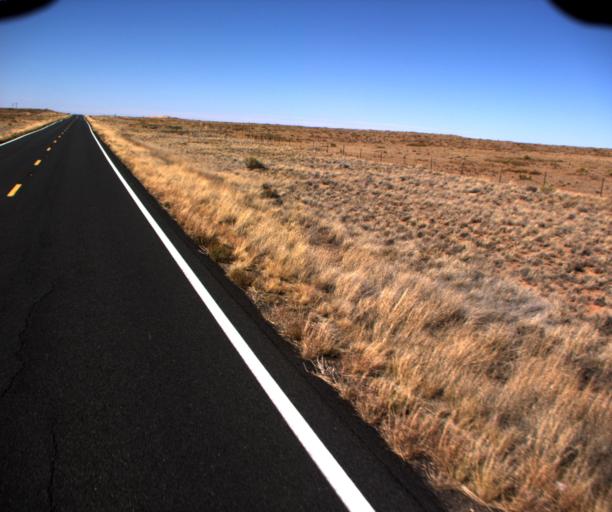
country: US
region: Arizona
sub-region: Coconino County
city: Tuba City
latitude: 35.9908
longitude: -111.0129
